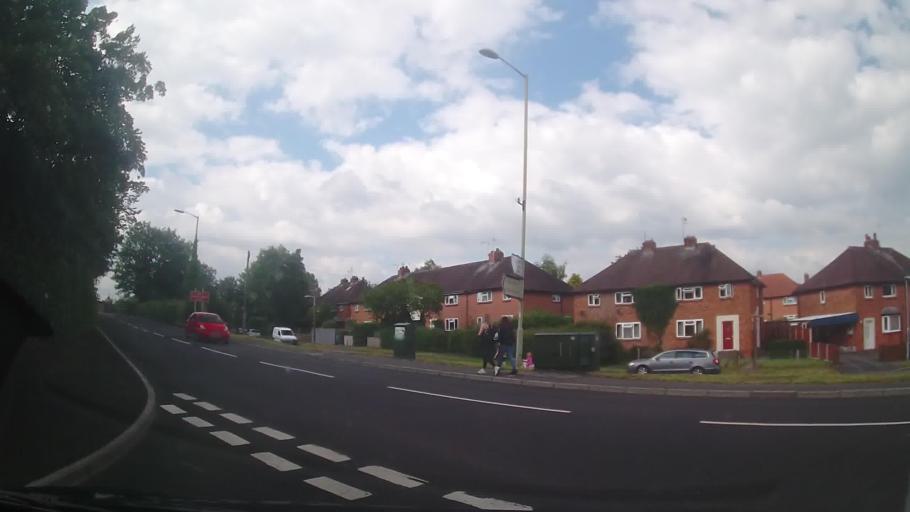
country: GB
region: England
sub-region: Shropshire
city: Oswestry
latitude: 52.8529
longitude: -3.0467
